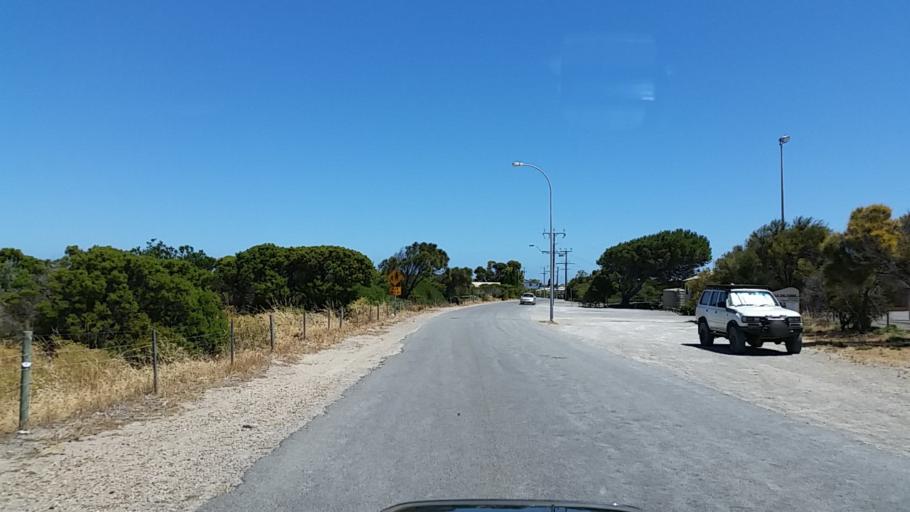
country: AU
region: South Australia
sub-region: Yorke Peninsula
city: Honiton
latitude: -35.2374
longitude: 136.9813
